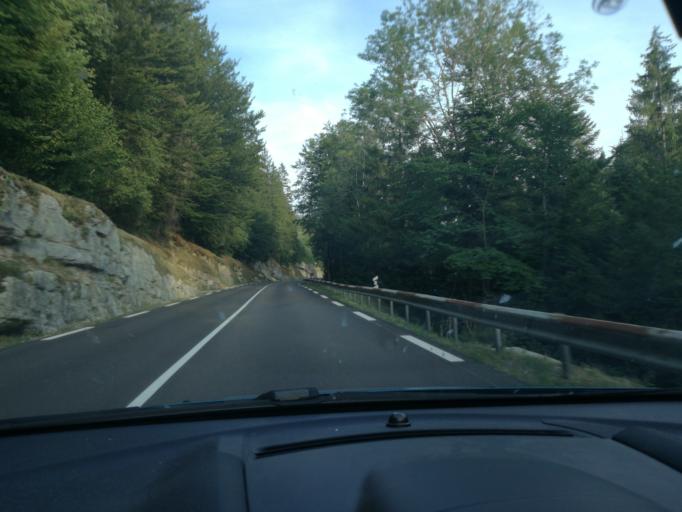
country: FR
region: Franche-Comte
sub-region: Departement du Jura
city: Morbier
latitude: 46.6247
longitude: 5.9574
